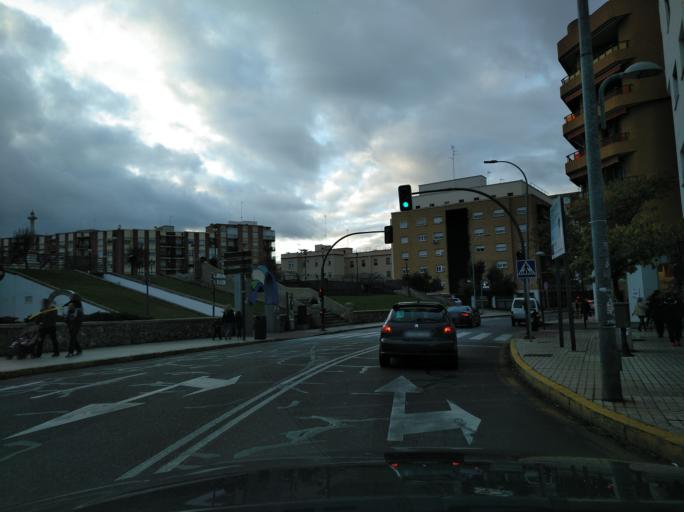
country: ES
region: Extremadura
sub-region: Provincia de Badajoz
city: Badajoz
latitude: 38.8757
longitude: -6.9752
